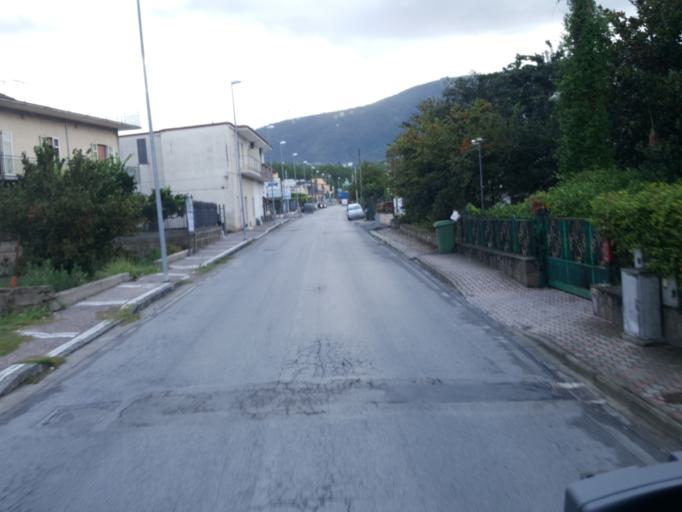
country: IT
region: Campania
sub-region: Provincia di Napoli
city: Palma Campania
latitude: 40.8791
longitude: 14.5558
